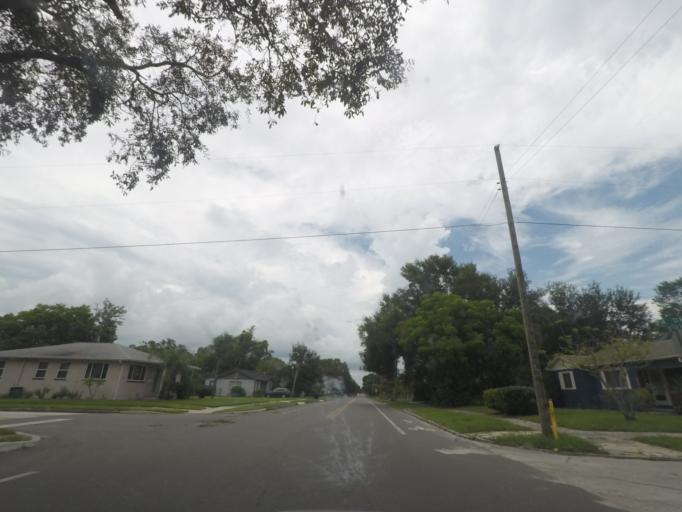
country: US
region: Florida
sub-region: Pinellas County
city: Lealman
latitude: 27.7993
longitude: -82.6525
